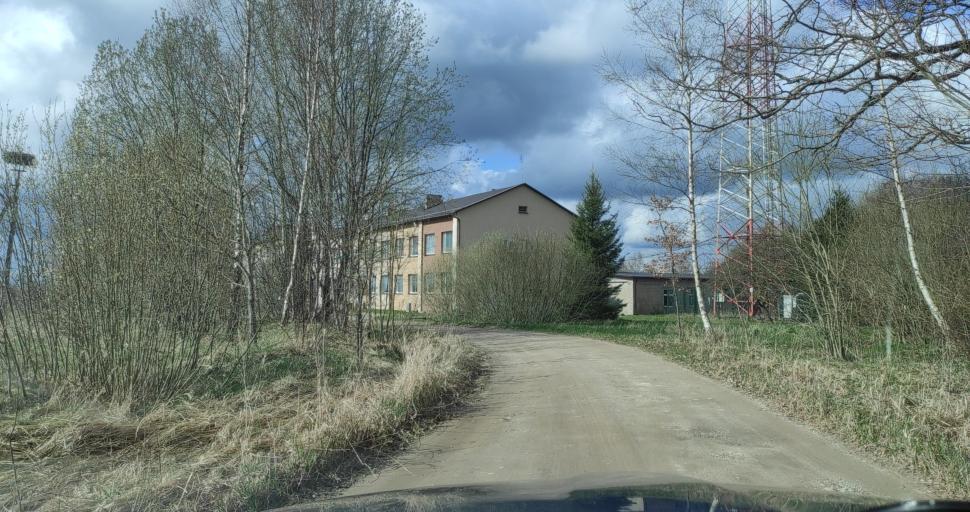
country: LV
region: Aizpute
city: Aizpute
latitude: 56.7122
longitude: 21.5949
